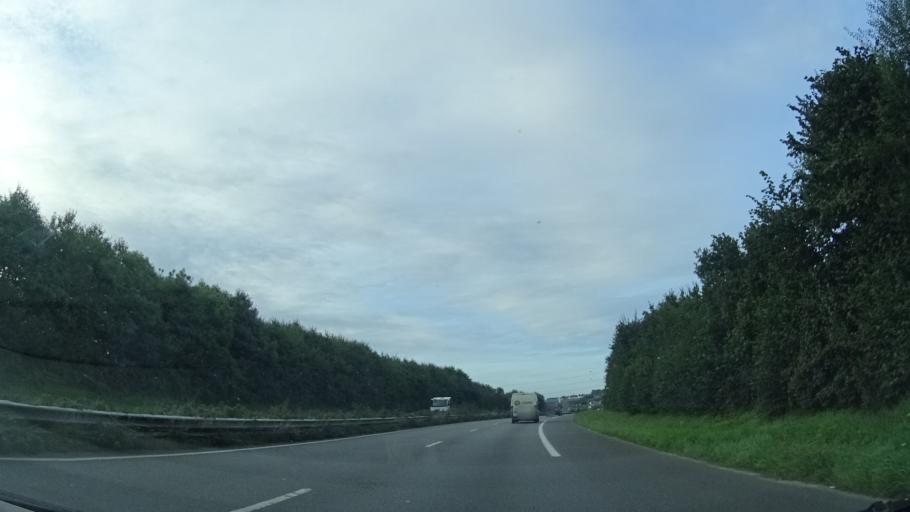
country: FR
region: Brittany
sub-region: Departement du Finistere
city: Gouesnou
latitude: 48.4271
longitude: -4.4371
